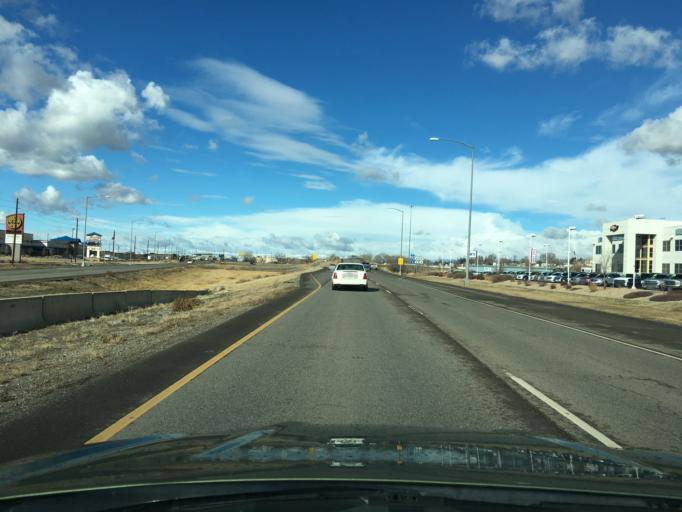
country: US
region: Colorado
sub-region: Mesa County
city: Grand Junction
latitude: 39.0747
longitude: -108.5745
